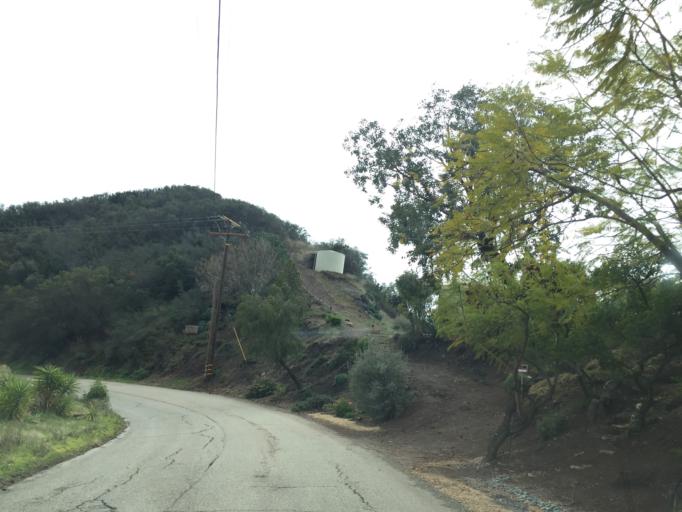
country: US
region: California
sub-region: Santa Barbara County
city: Goleta
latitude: 34.4801
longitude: -119.7978
